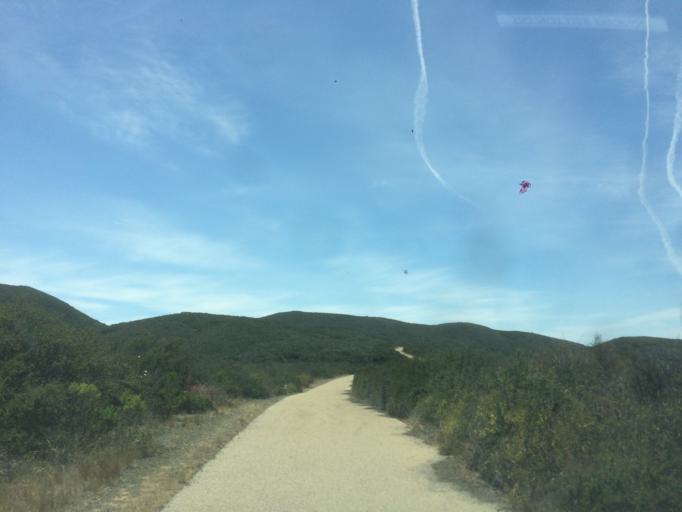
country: US
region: California
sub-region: San Luis Obispo County
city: San Luis Obispo
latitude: 35.2529
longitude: -120.7053
